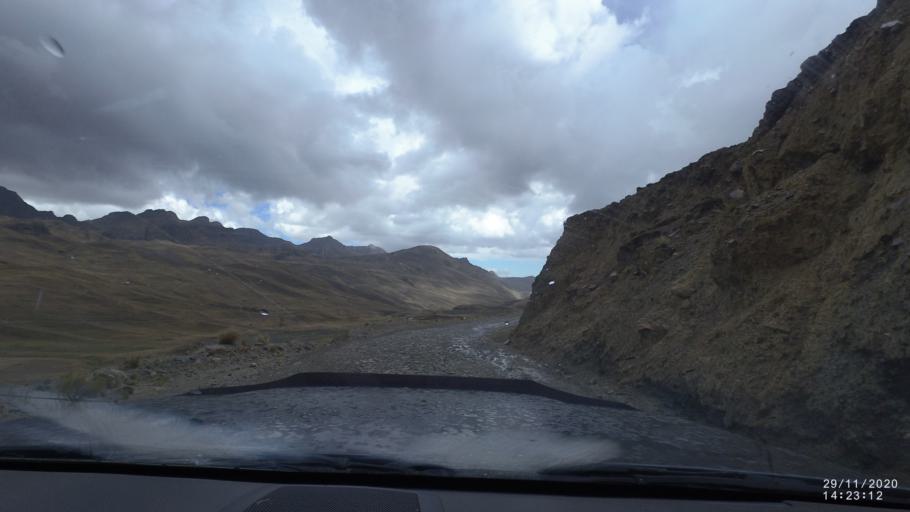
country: BO
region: Cochabamba
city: Sipe Sipe
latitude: -17.2541
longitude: -66.3849
